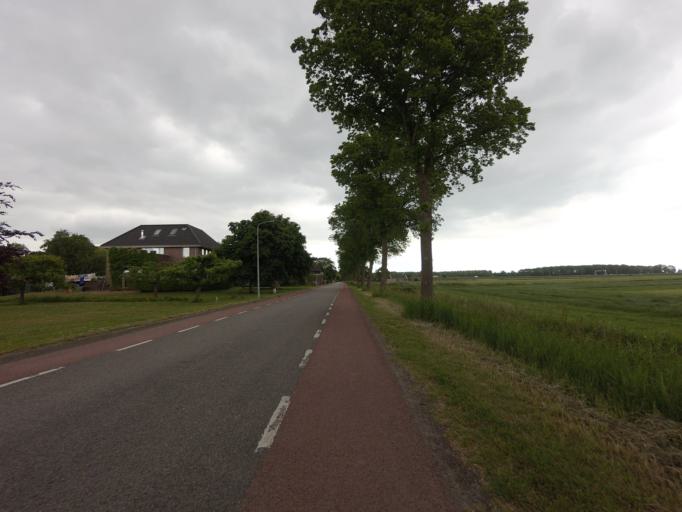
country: NL
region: North Holland
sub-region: Gemeente Hoorn
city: Hoorn
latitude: 52.6197
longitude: 4.9952
